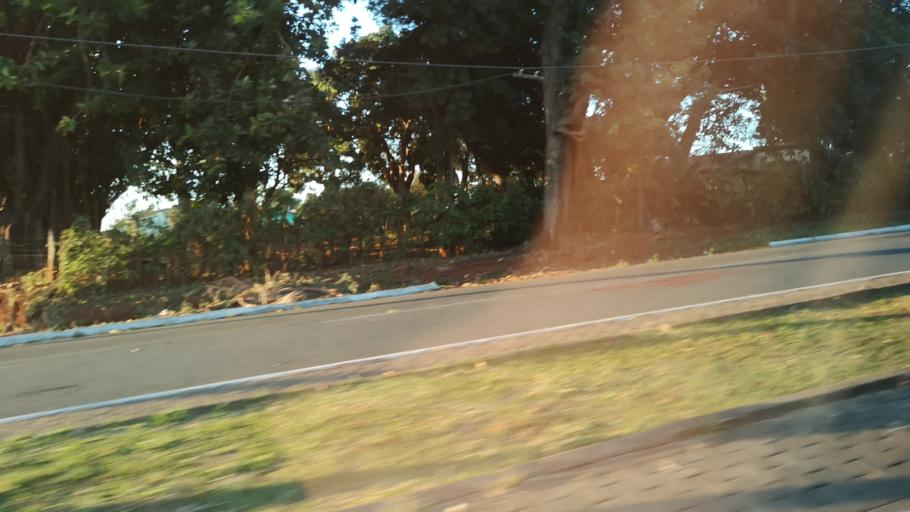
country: BR
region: Goias
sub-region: Senador Canedo
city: Senador Canedo
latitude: -16.6913
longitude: -49.0955
